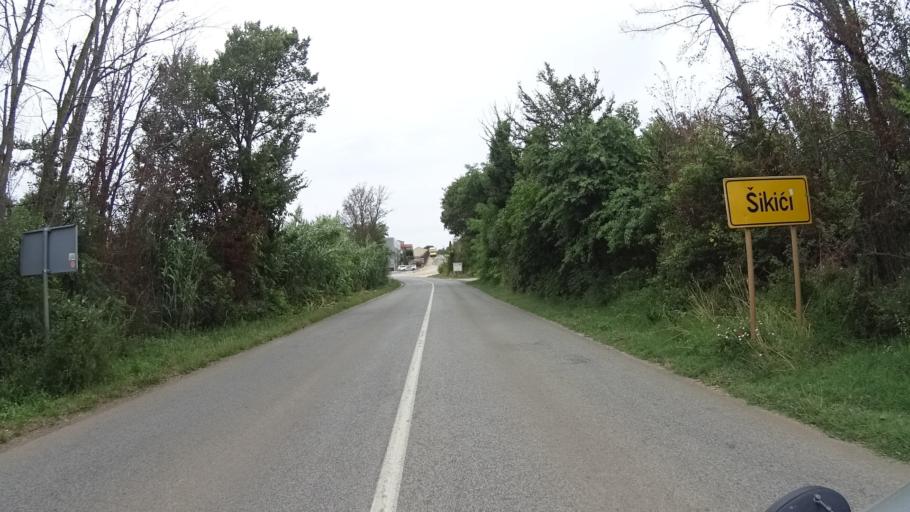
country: HR
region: Istarska
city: Medulin
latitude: 44.8596
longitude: 13.9051
